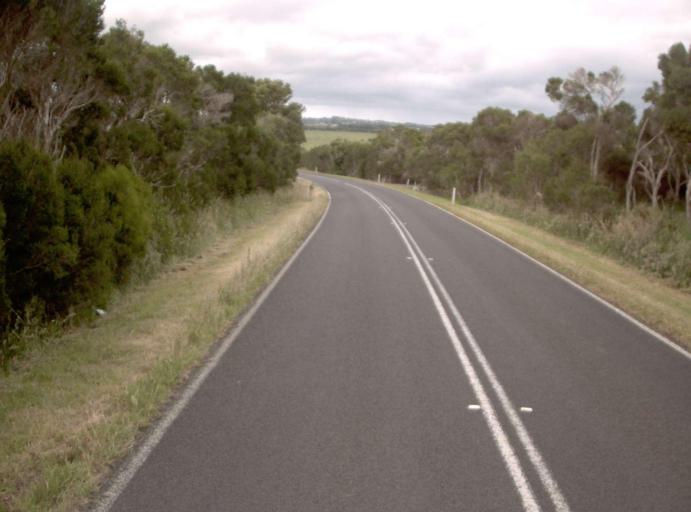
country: AU
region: Victoria
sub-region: Bass Coast
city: North Wonthaggi
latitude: -38.5606
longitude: 145.6347
